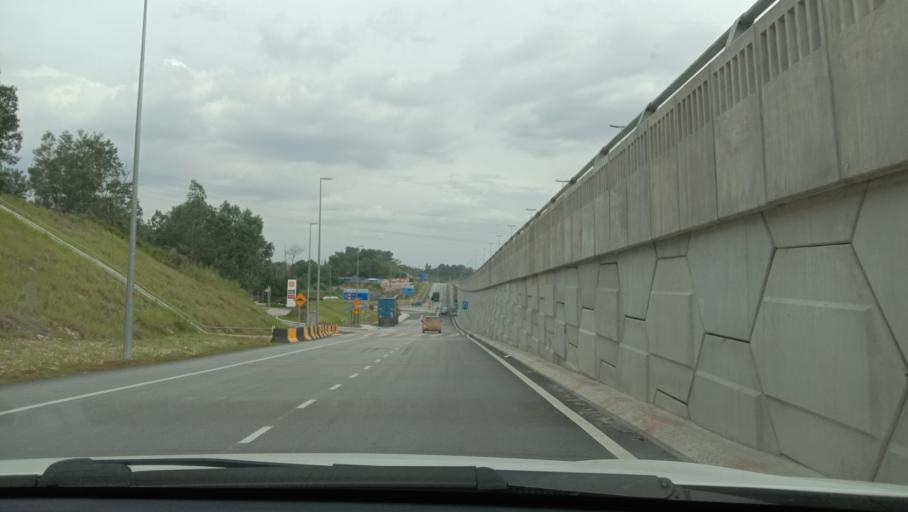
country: MY
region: Selangor
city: Kampung Baru Subang
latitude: 3.1267
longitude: 101.5180
